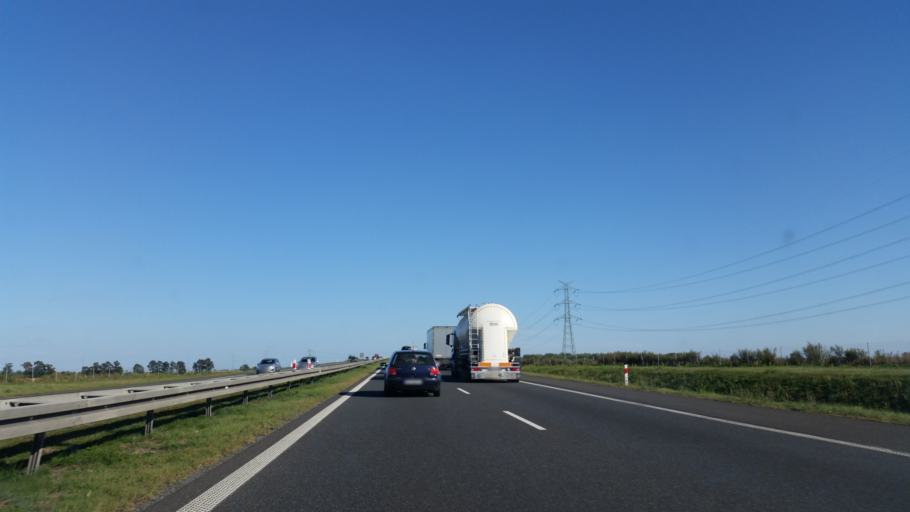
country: PL
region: Opole Voivodeship
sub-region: Powiat brzeski
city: Olszanka
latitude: 50.7522
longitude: 17.4389
